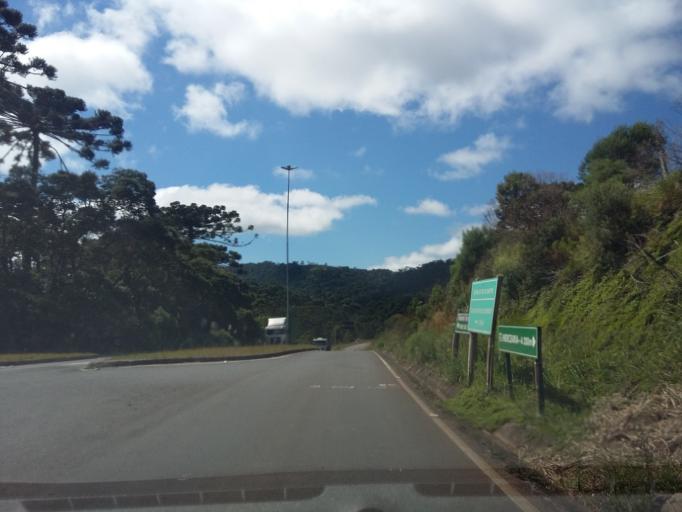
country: BR
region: Santa Catarina
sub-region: Sao Joaquim
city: Sao Joaquim
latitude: -28.2321
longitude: -49.8256
